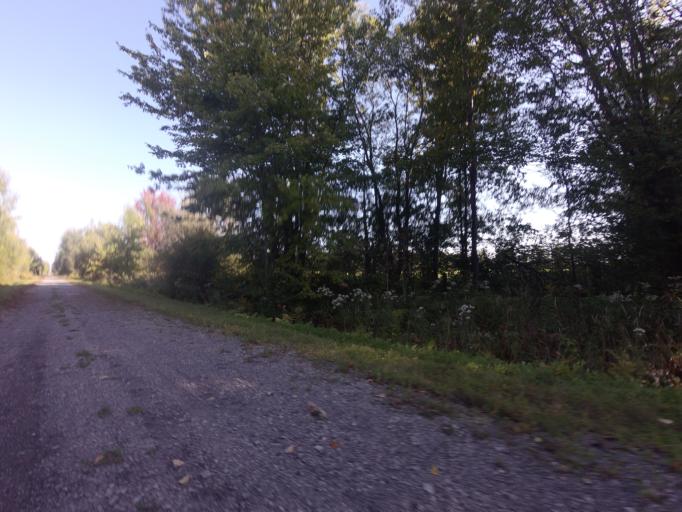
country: CA
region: Ontario
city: Hawkesbury
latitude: 45.5363
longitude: -74.6011
